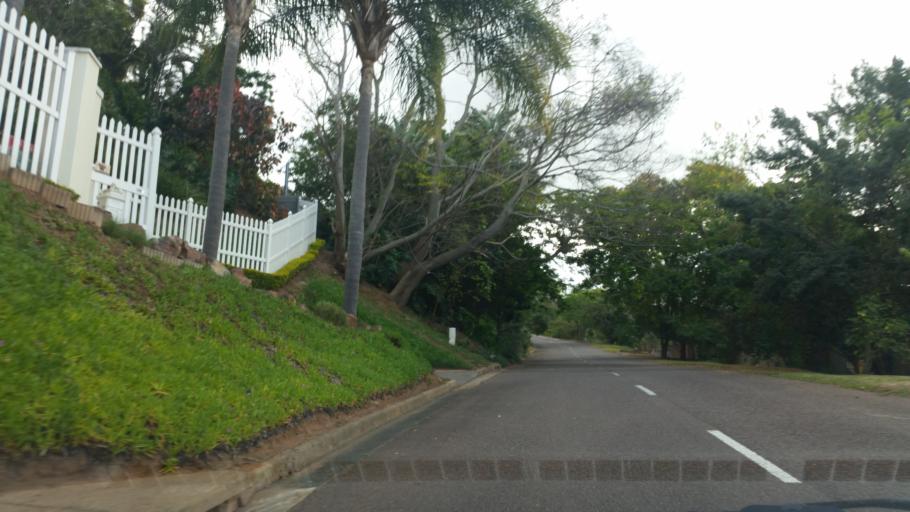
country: ZA
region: KwaZulu-Natal
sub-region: eThekwini Metropolitan Municipality
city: Berea
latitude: -29.8215
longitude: 30.9367
